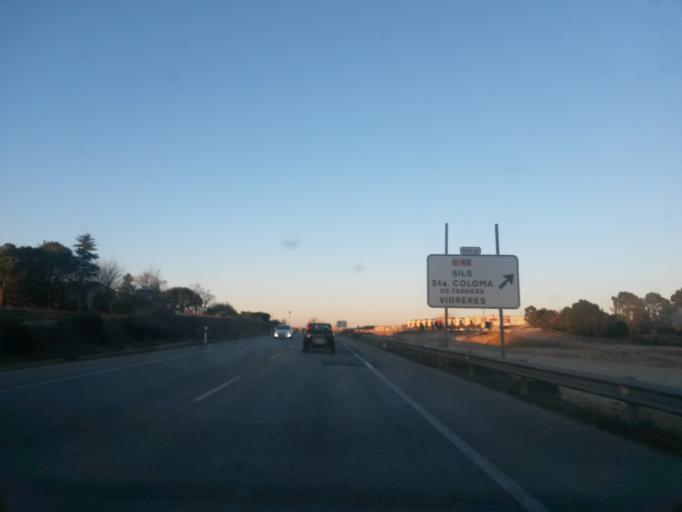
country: ES
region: Catalonia
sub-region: Provincia de Girona
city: Sils
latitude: 41.7960
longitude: 2.7592
